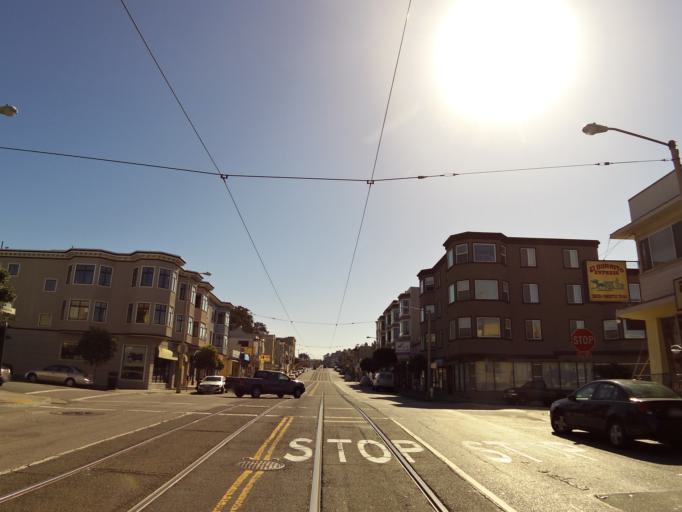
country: US
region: California
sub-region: San Mateo County
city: Daly City
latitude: 37.7427
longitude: -122.4835
